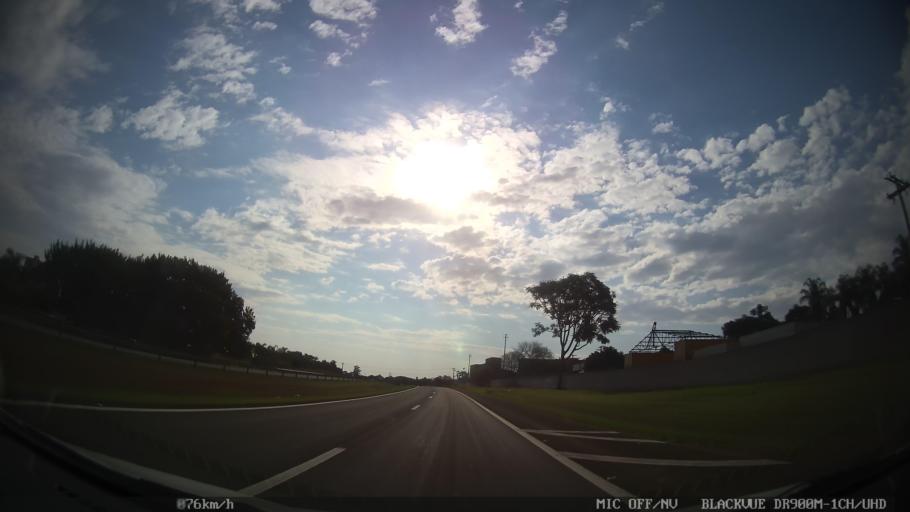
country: BR
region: Sao Paulo
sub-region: Paulinia
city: Paulinia
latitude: -22.7555
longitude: -47.1465
